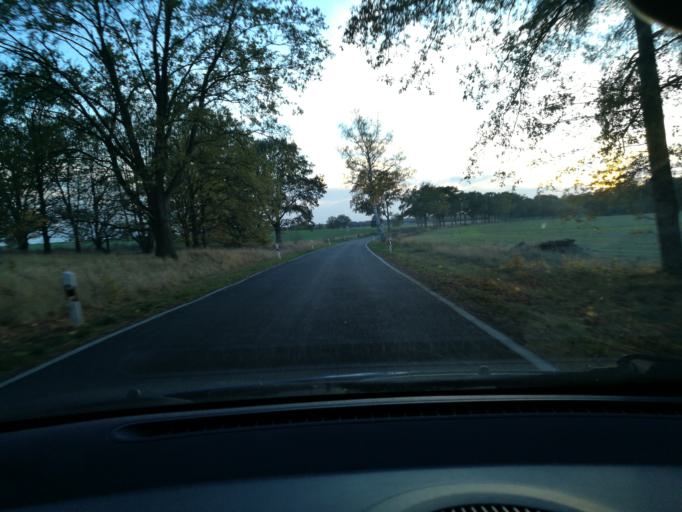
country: DE
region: Brandenburg
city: Cumlosen
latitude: 53.0968
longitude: 11.6848
